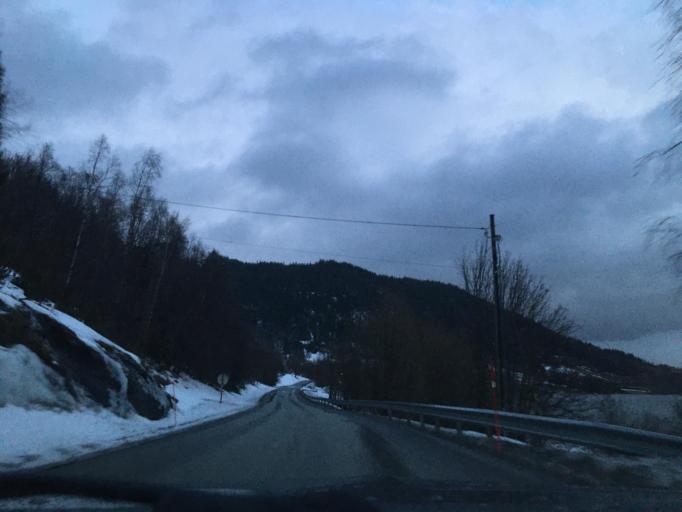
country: NO
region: Nordland
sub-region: Rana
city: Hauknes
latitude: 66.3091
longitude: 13.9874
